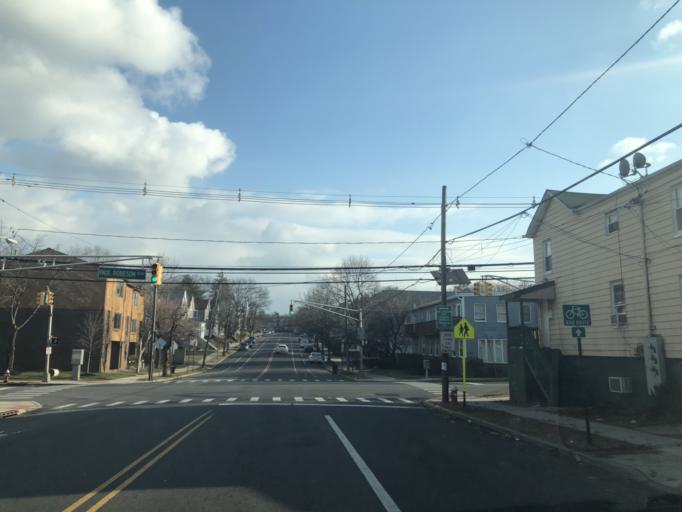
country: US
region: New Jersey
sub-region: Middlesex County
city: New Brunswick
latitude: 40.4857
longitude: -74.4421
